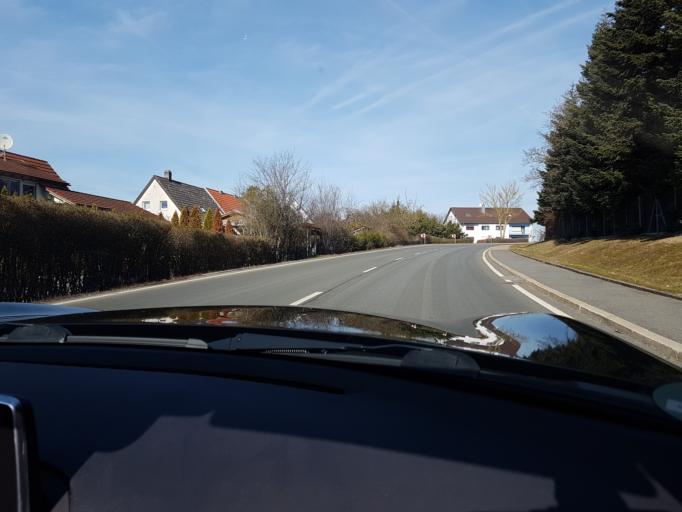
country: DE
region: Baden-Wuerttemberg
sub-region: Karlsruhe Region
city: Osterburken
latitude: 49.4304
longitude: 9.4364
